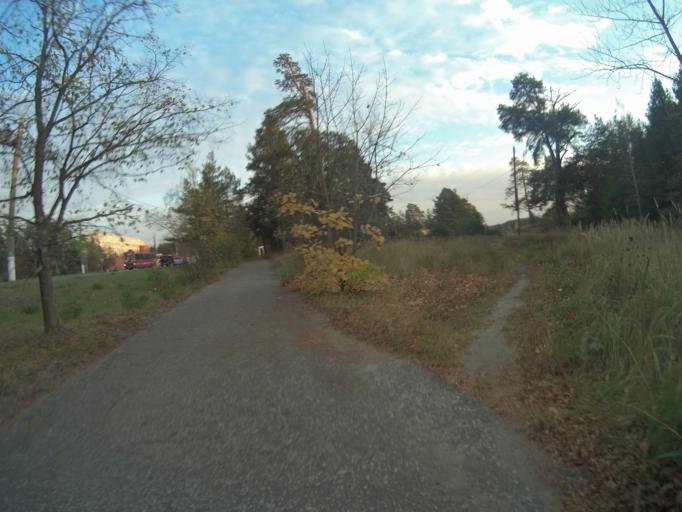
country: RU
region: Vladimir
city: Kommunar
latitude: 56.1038
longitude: 40.4364
